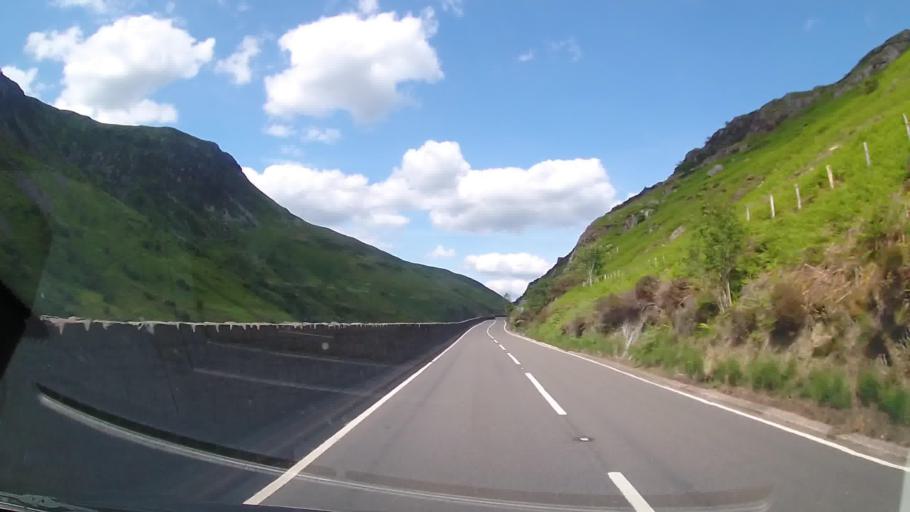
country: GB
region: Wales
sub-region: Gwynedd
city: Corris
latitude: 52.6945
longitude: -3.8618
